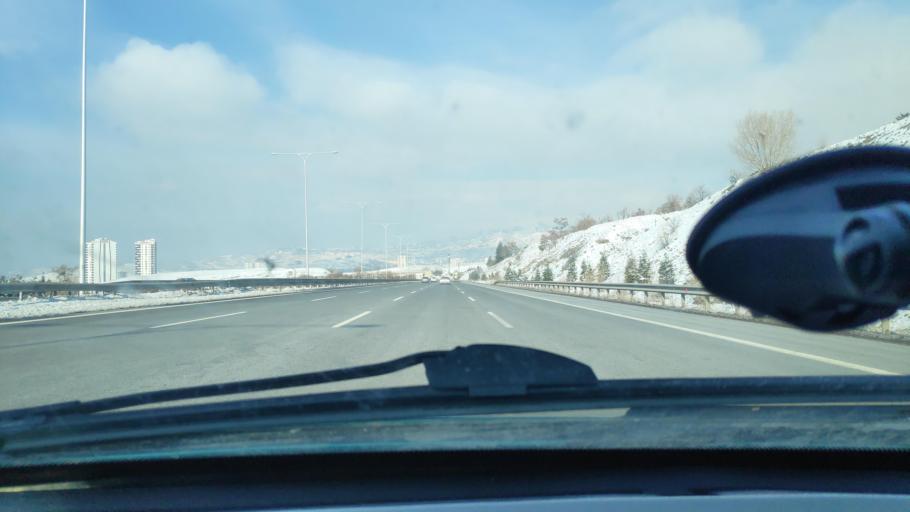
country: TR
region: Ankara
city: Batikent
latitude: 40.0203
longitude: 32.8140
